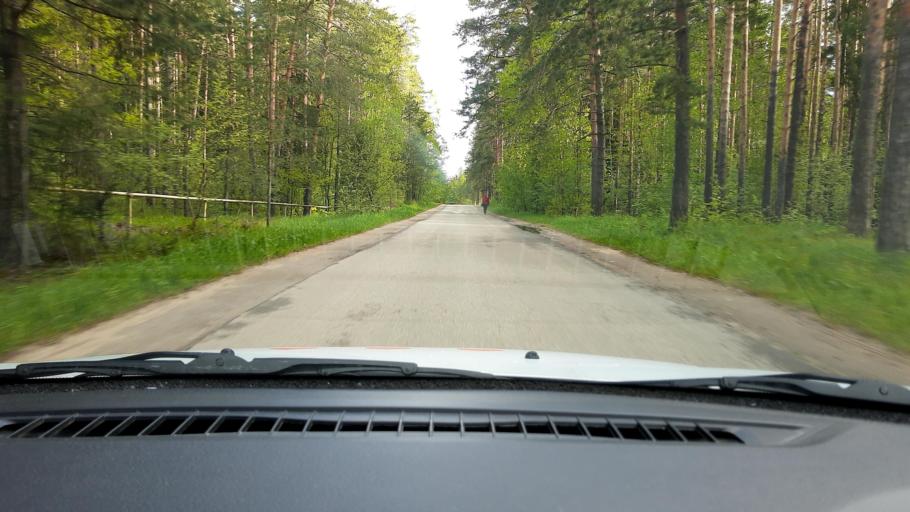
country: RU
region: Nizjnij Novgorod
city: Afonino
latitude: 56.1832
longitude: 44.0799
